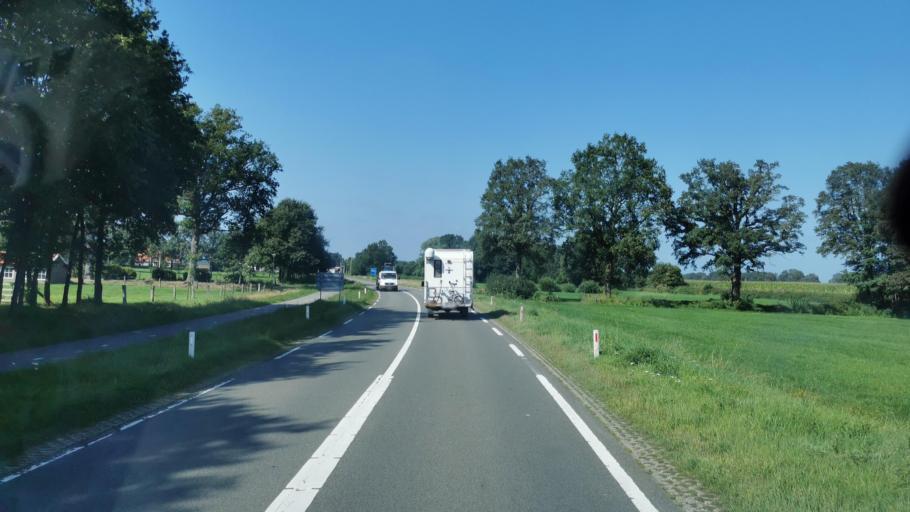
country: NL
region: Overijssel
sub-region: Gemeente Oldenzaal
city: Oldenzaal
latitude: 52.3476
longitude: 6.9321
